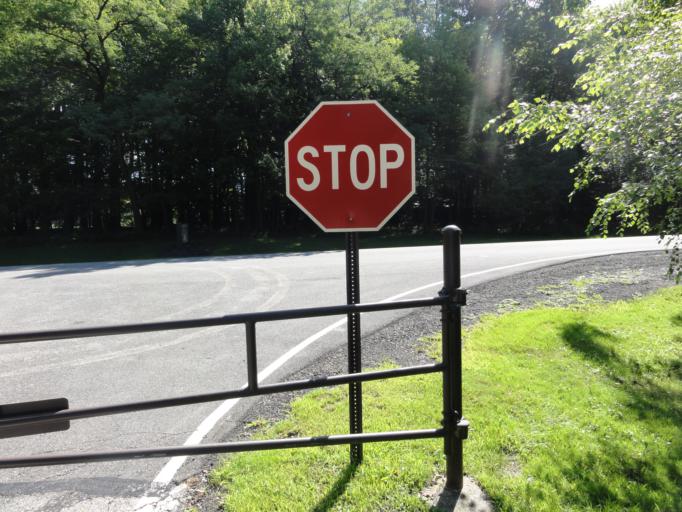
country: US
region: Ohio
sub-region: Cuyahoga County
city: Bedford
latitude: 41.3811
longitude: -81.5476
